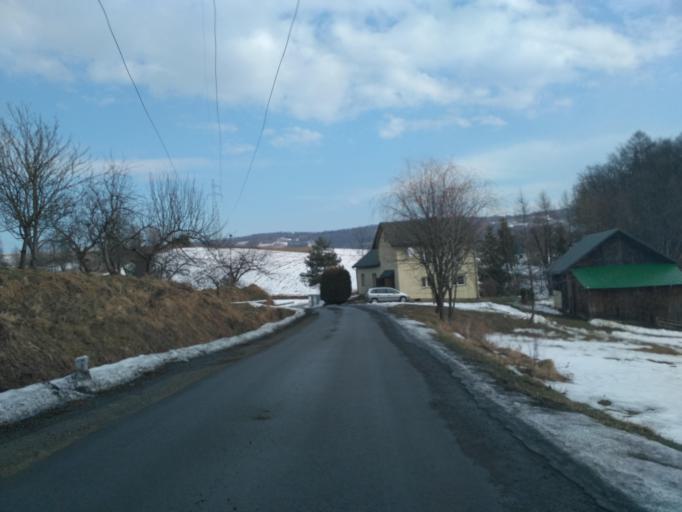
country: PL
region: Subcarpathian Voivodeship
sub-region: Powiat brzozowski
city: Niebocko
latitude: 49.6507
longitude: 22.1306
